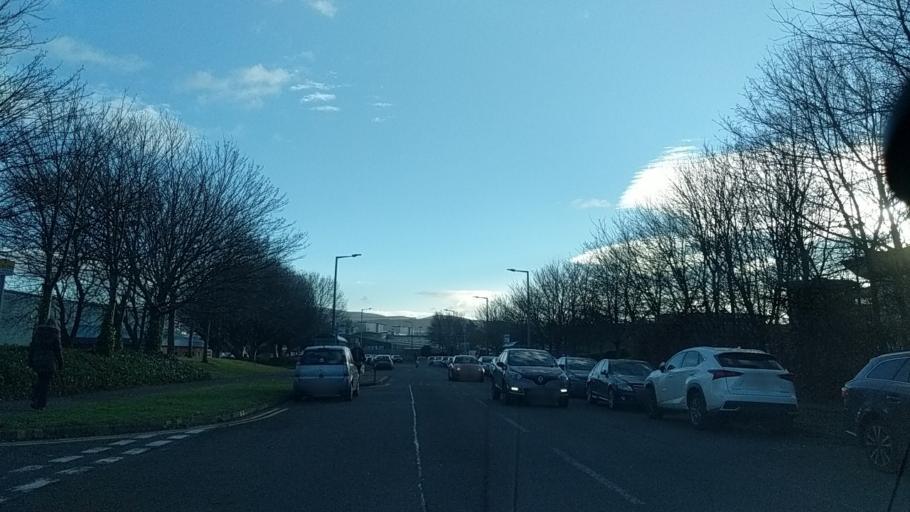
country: GB
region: Scotland
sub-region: Edinburgh
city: Currie
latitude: 55.9316
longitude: -3.3059
